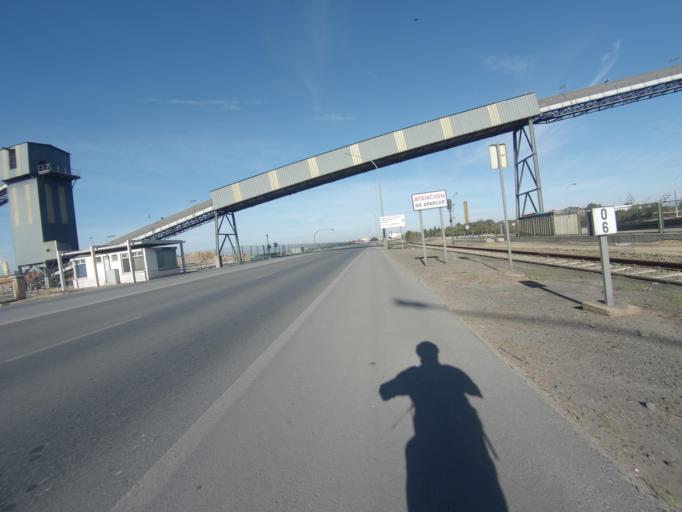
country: ES
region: Andalusia
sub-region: Provincia de Huelva
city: Punta Umbria
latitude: 37.1968
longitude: -6.9335
